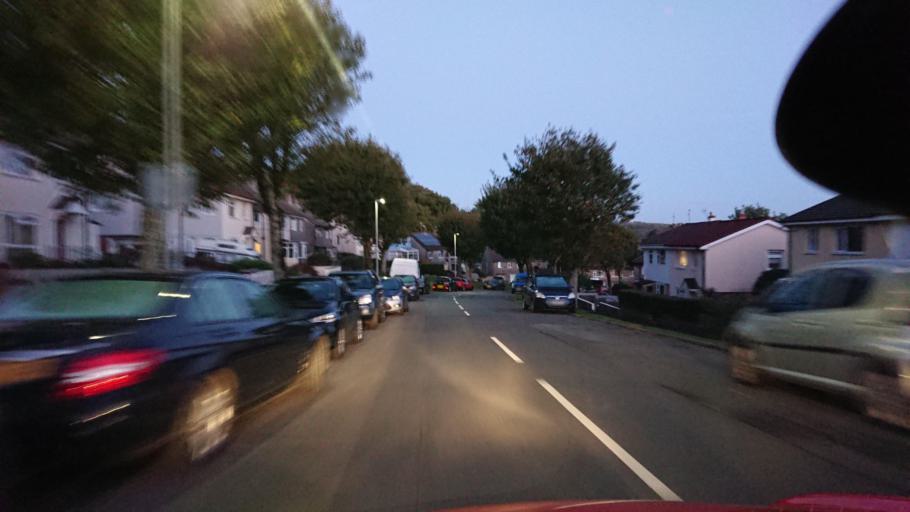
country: GB
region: England
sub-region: Plymouth
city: Plymstock
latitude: 50.3901
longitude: -4.0968
